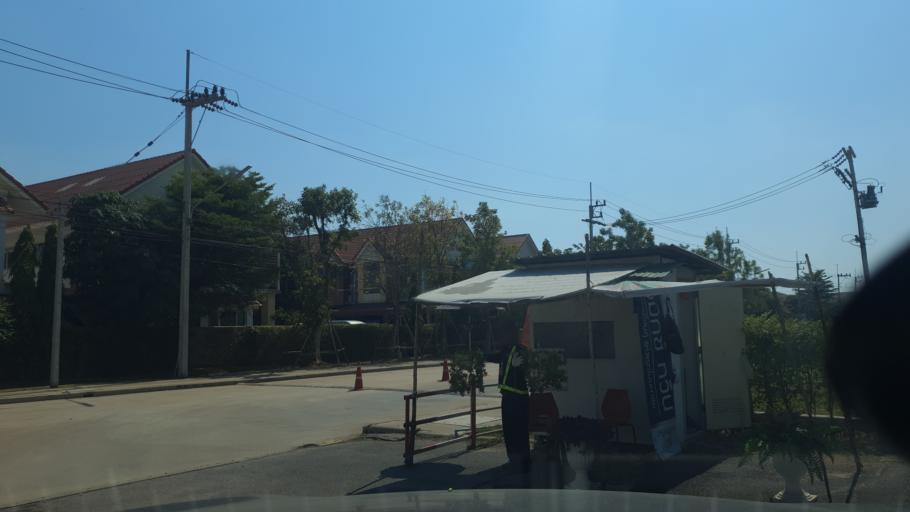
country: TH
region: Samut Sakhon
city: Samut Sakhon
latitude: 13.5287
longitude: 100.2017
